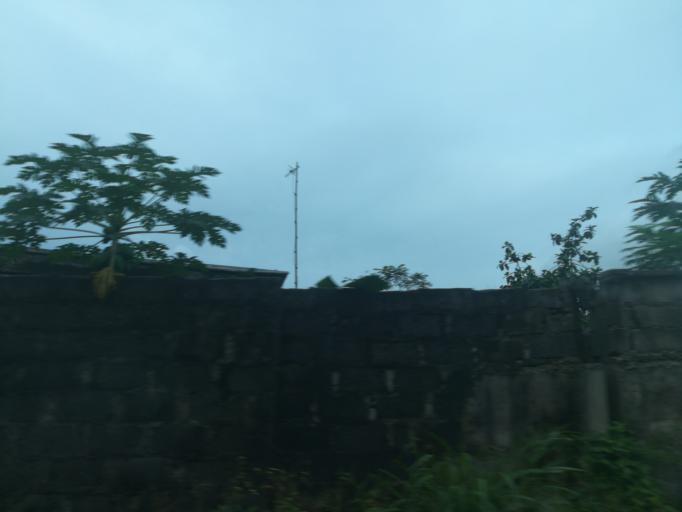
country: NG
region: Rivers
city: Port Harcourt
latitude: 4.8189
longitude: 6.9852
